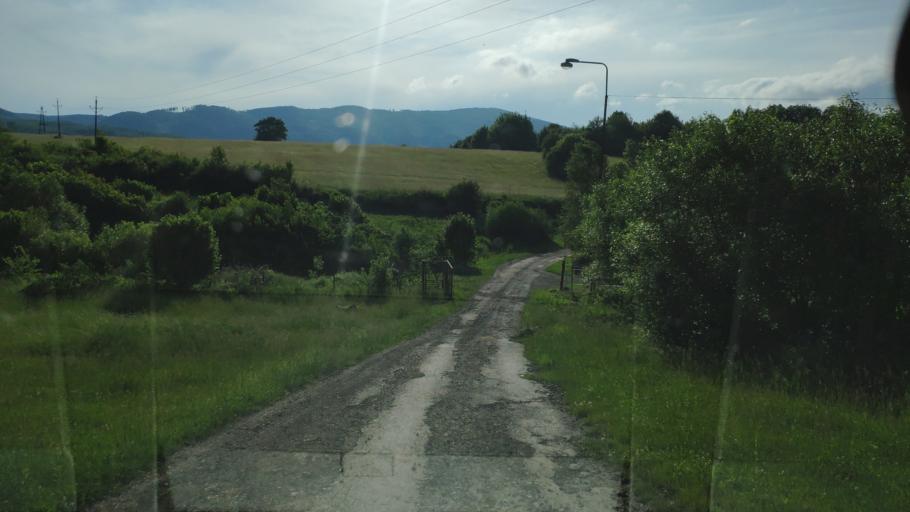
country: SK
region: Presovsky
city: Vranov nad Topl'ou
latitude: 48.8257
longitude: 21.5782
